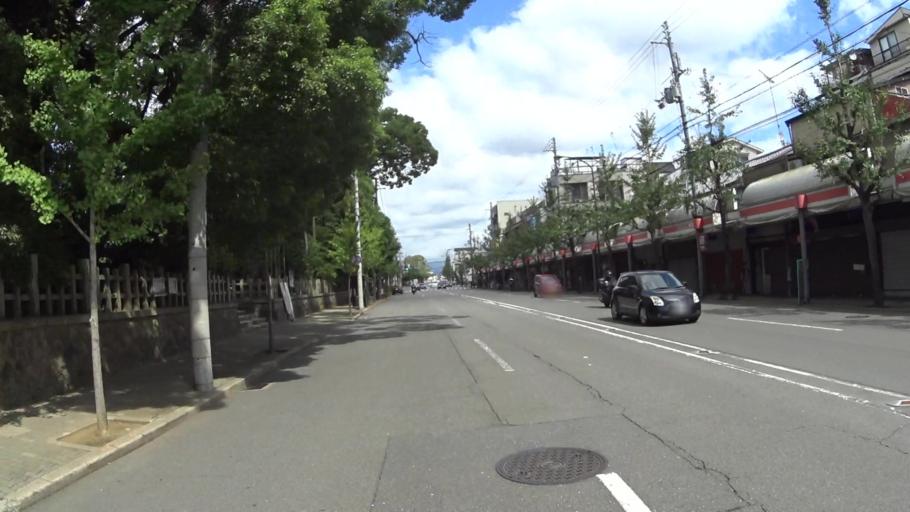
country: JP
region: Kyoto
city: Kyoto
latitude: 34.9842
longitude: 135.7739
